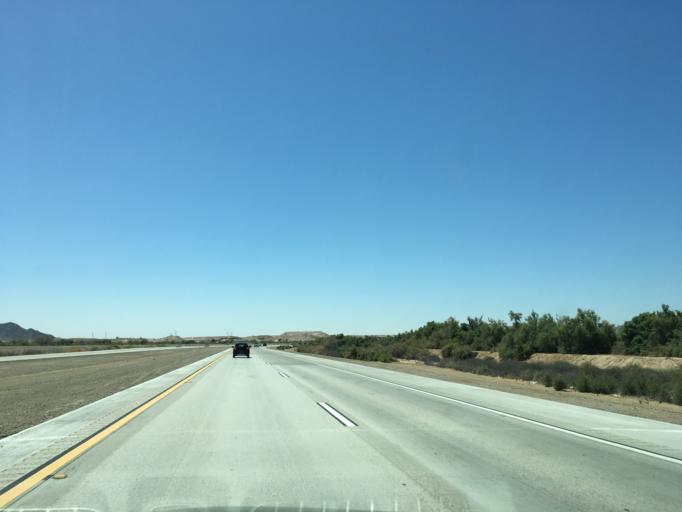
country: US
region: Arizona
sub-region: Yuma County
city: Yuma
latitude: 32.7411
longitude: -114.6812
